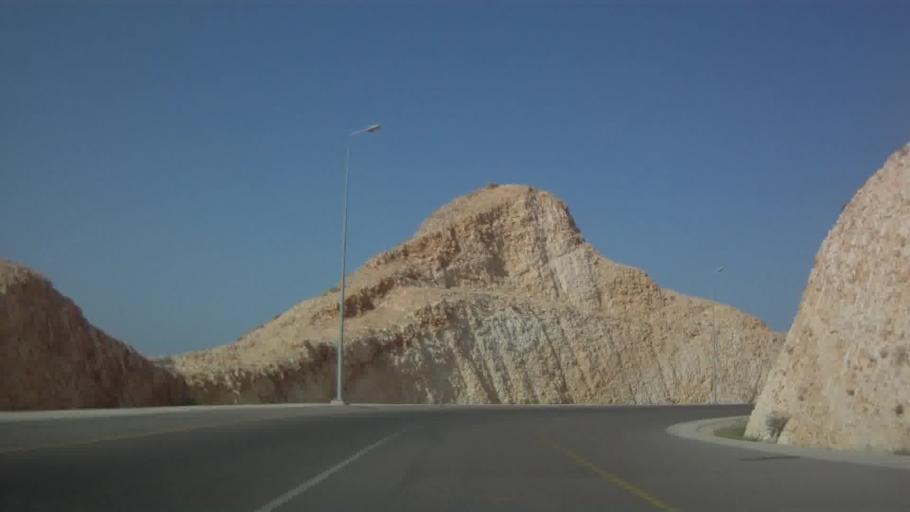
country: OM
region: Muhafazat Masqat
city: Muscat
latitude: 23.5436
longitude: 58.6519
